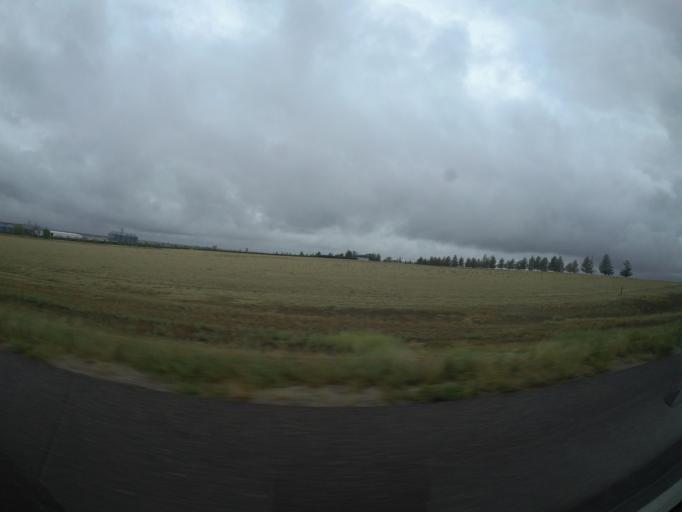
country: US
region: Colorado
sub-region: Arapahoe County
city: Byers
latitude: 39.7409
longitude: -104.1205
